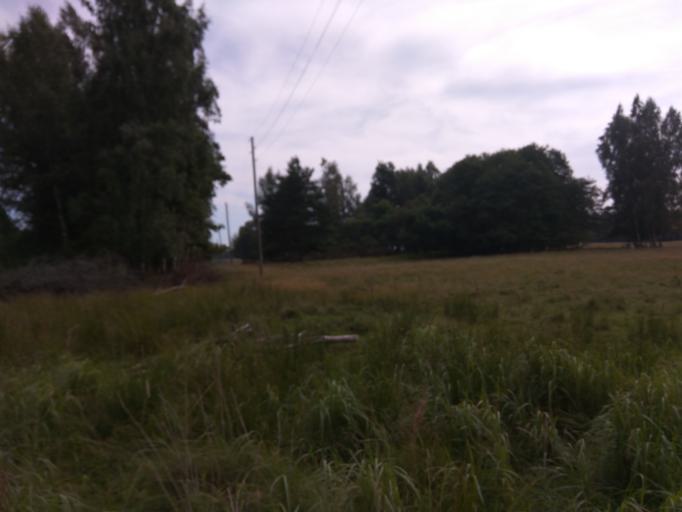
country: LV
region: Alsunga
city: Alsunga
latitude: 56.9819
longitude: 21.6883
